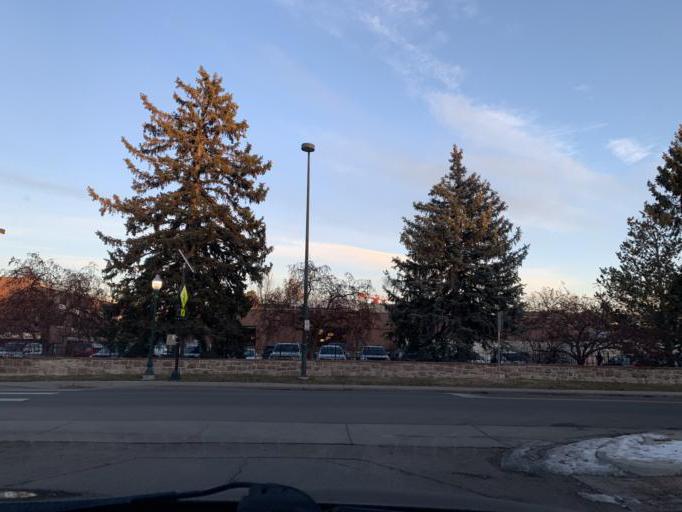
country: US
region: Colorado
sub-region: Adams County
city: Berkley
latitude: 39.7893
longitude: -105.0348
